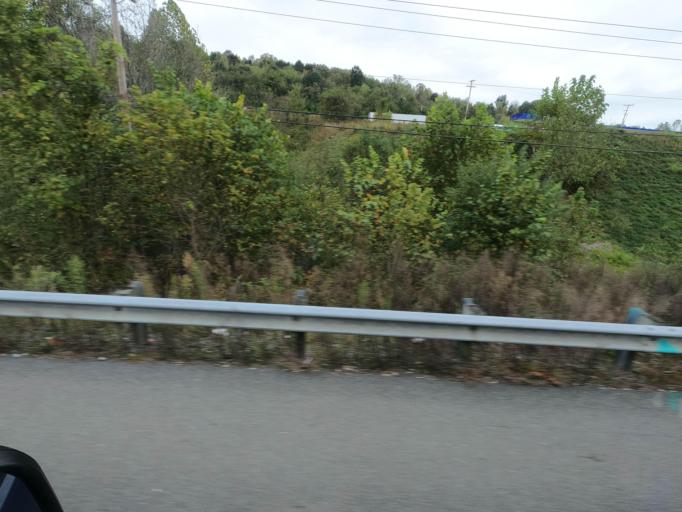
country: US
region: Tennessee
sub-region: Sullivan County
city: Kingsport
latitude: 36.5553
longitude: -82.6074
